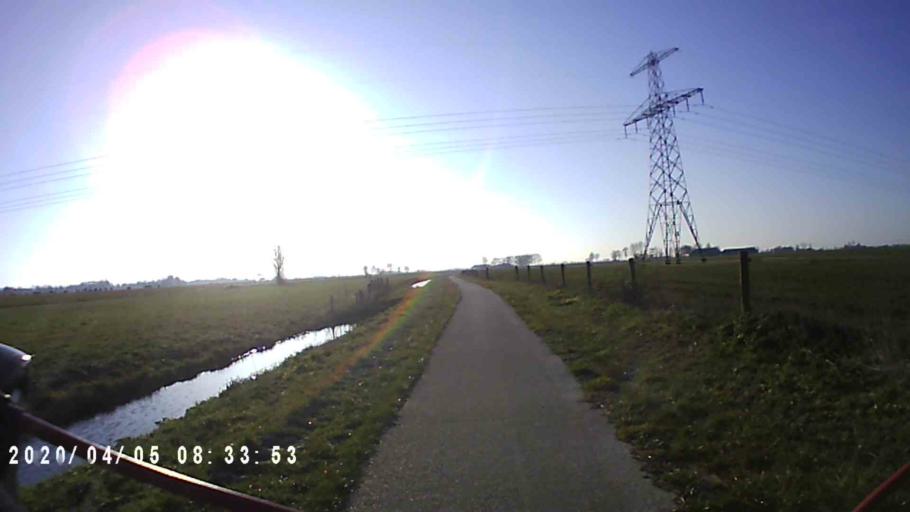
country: NL
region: Groningen
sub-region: Gemeente Winsum
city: Winsum
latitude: 53.3243
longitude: 6.4930
